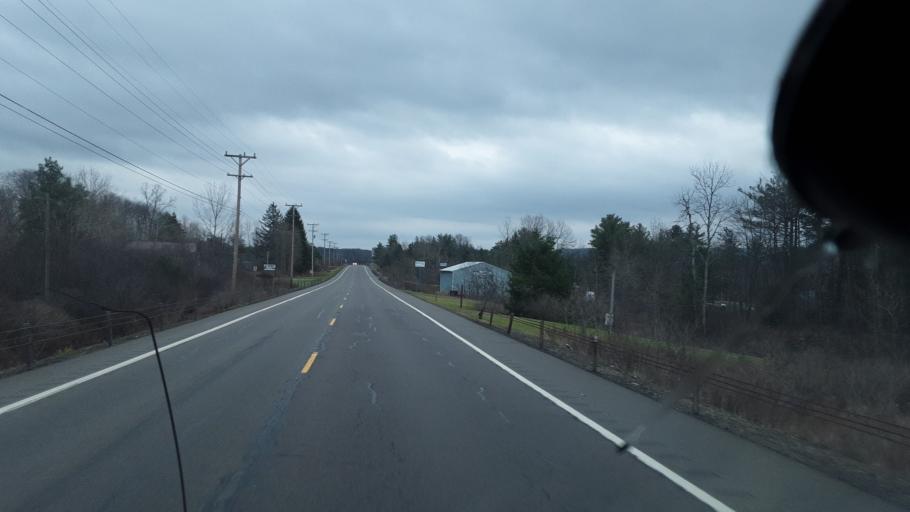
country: US
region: New York
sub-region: Allegany County
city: Houghton
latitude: 42.3892
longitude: -78.2161
